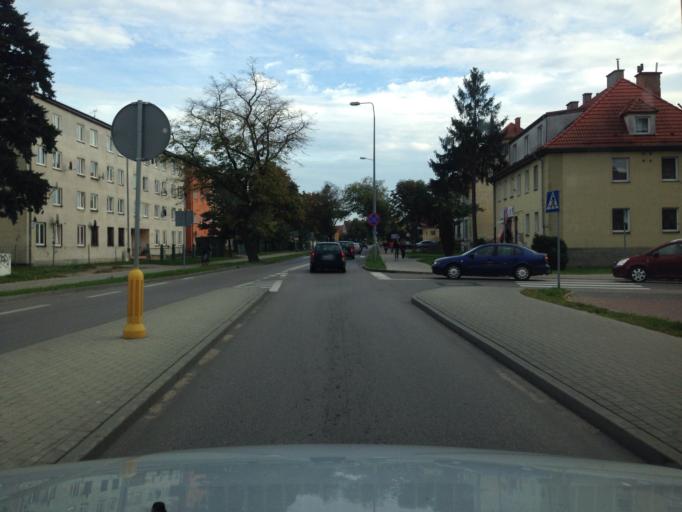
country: PL
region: Pomeranian Voivodeship
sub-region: Powiat leborski
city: Lebork
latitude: 54.5316
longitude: 17.7603
